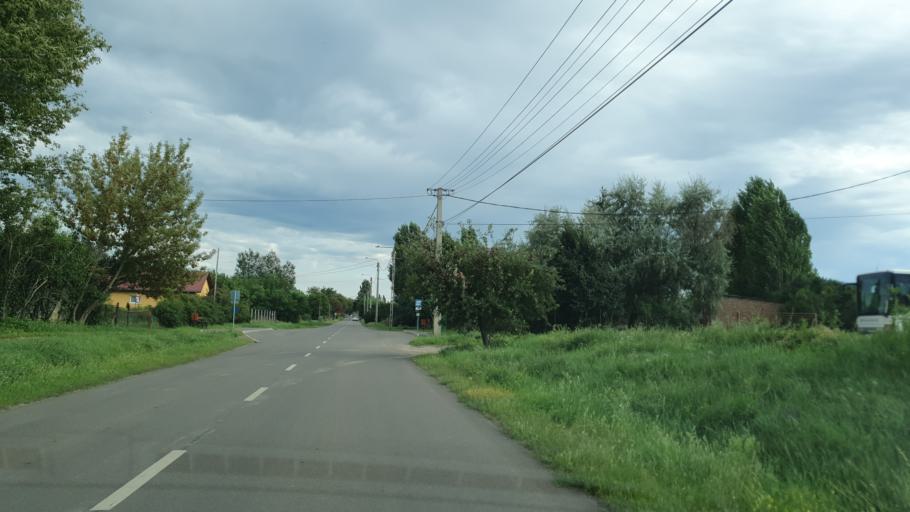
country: HU
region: Heves
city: Zagyvaszanto
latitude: 47.7694
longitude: 19.6698
